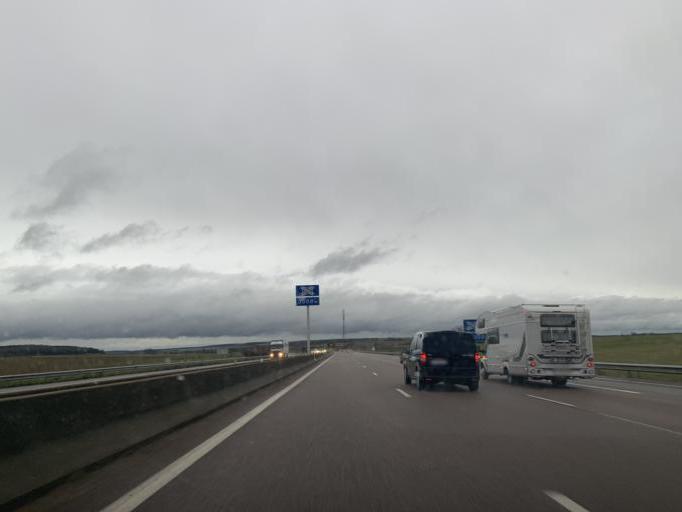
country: FR
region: Champagne-Ardenne
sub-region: Departement de la Haute-Marne
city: Rolampont
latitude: 47.8816
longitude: 5.2212
